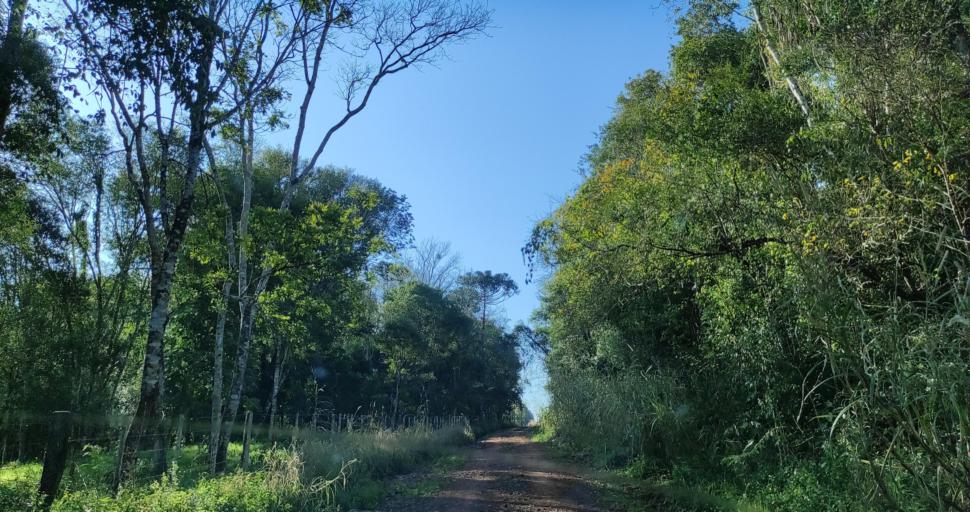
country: AR
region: Misiones
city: Capiovi
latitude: -26.8965
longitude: -55.1071
